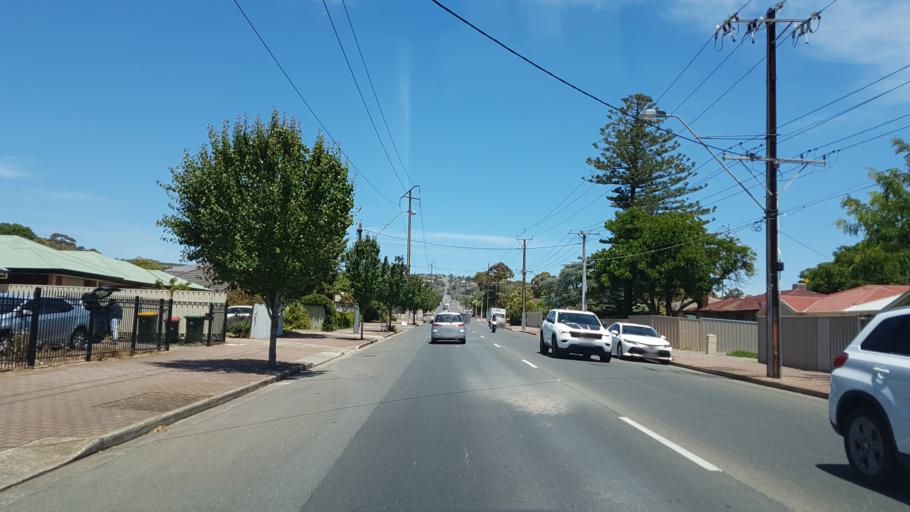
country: AU
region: South Australia
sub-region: Marion
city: Sturt
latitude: -35.0224
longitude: 138.5412
